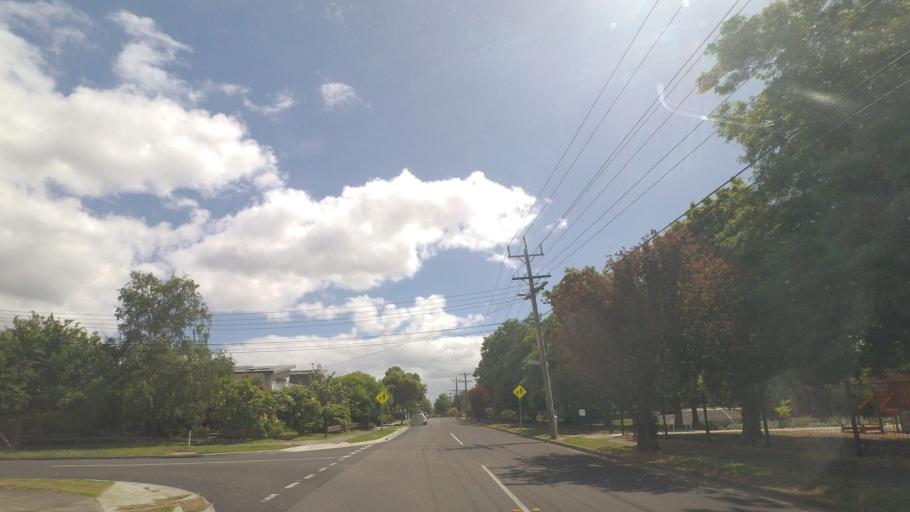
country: AU
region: Victoria
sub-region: Knox
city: Boronia
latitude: -37.8598
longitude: 145.2784
